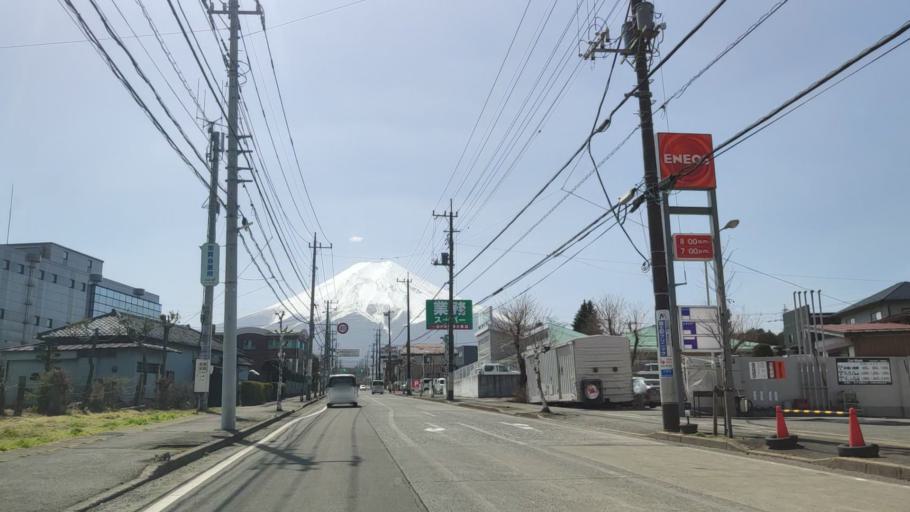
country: JP
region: Yamanashi
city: Fujikawaguchiko
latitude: 35.4759
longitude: 138.8004
